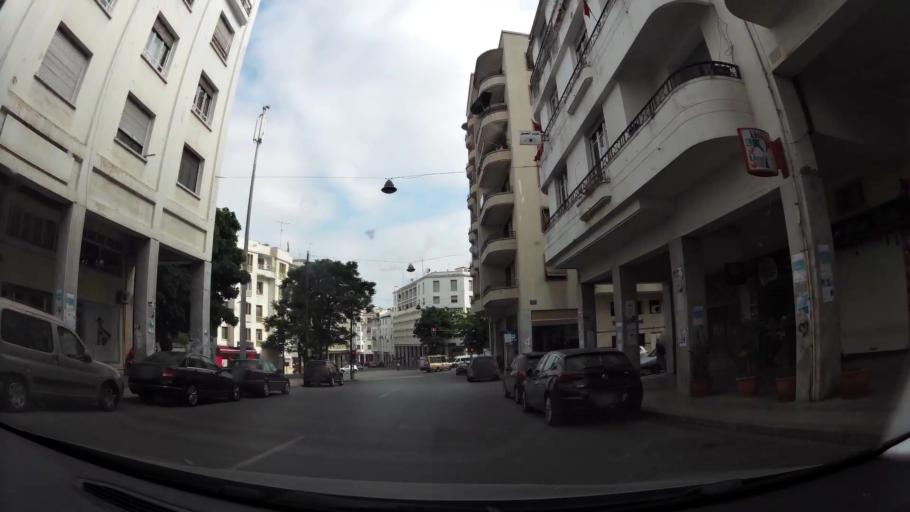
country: MA
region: Rabat-Sale-Zemmour-Zaer
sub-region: Rabat
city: Rabat
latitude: 34.0178
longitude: -6.8341
